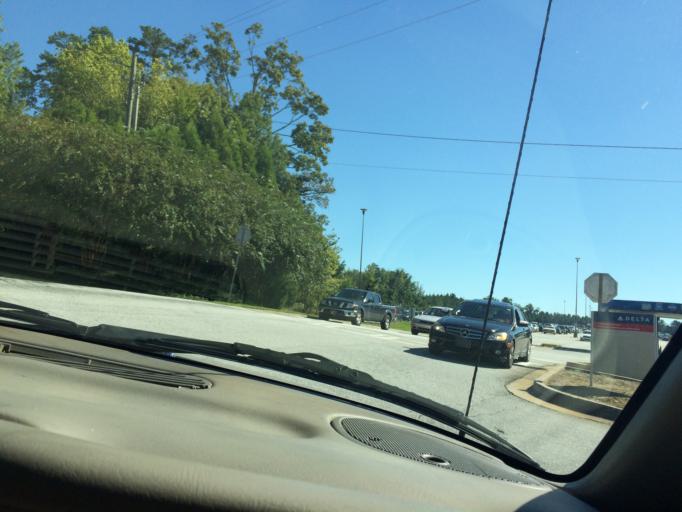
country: US
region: Georgia
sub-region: Fulton County
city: College Park
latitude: 33.6484
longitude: -84.4623
